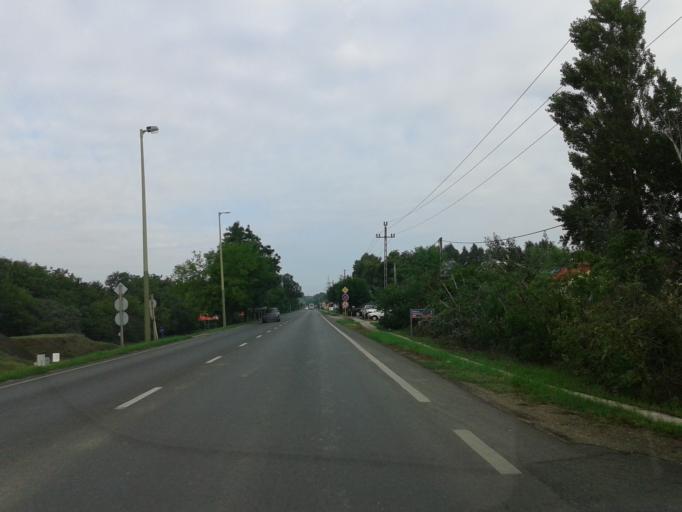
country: HU
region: Csongrad
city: Szeged
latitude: 46.2364
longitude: 20.1707
